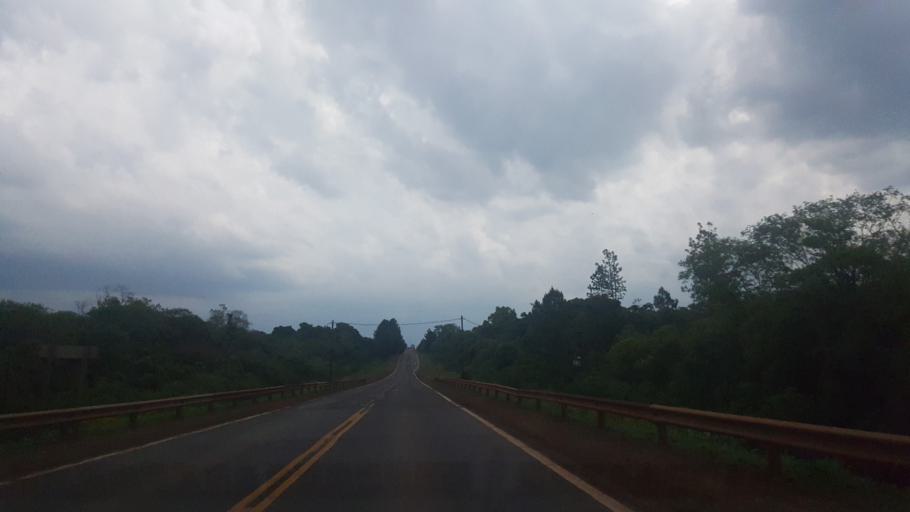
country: AR
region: Misiones
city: Santo Pipo
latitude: -27.1209
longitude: -55.3737
